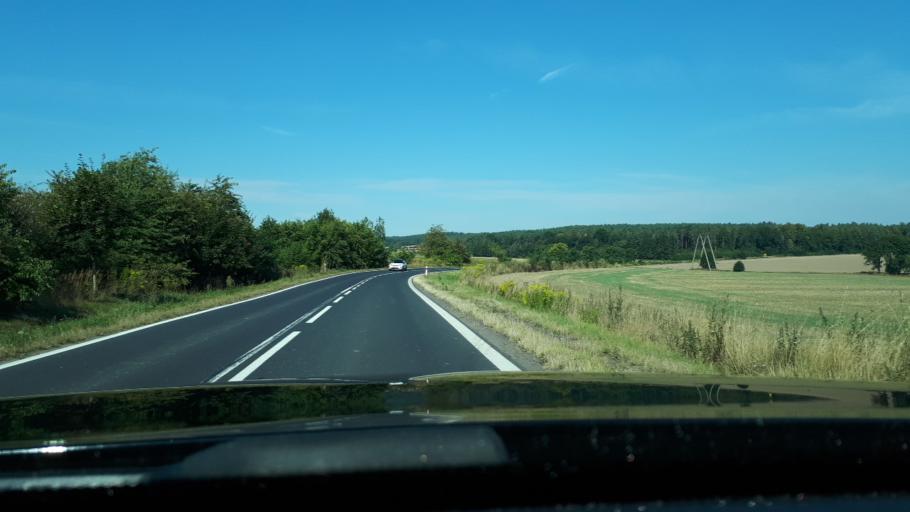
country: PL
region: Lower Silesian Voivodeship
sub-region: Powiat lubanski
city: Pisarzowice
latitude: 51.1810
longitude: 15.2585
